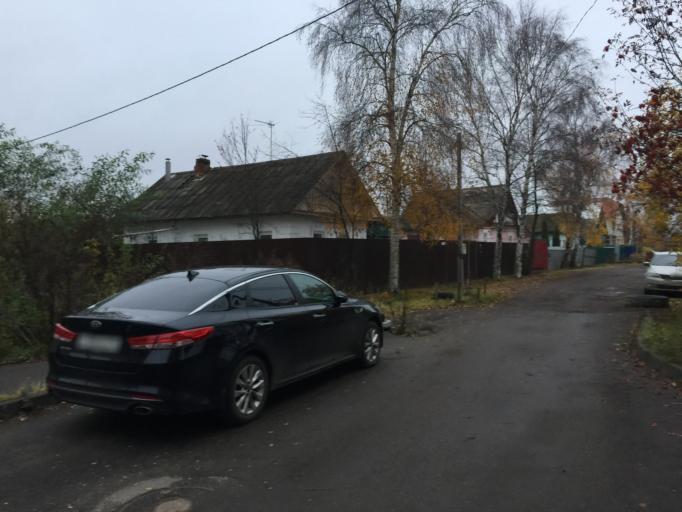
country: RU
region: Jaroslavl
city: Yaroslavl
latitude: 57.7199
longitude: 39.7733
